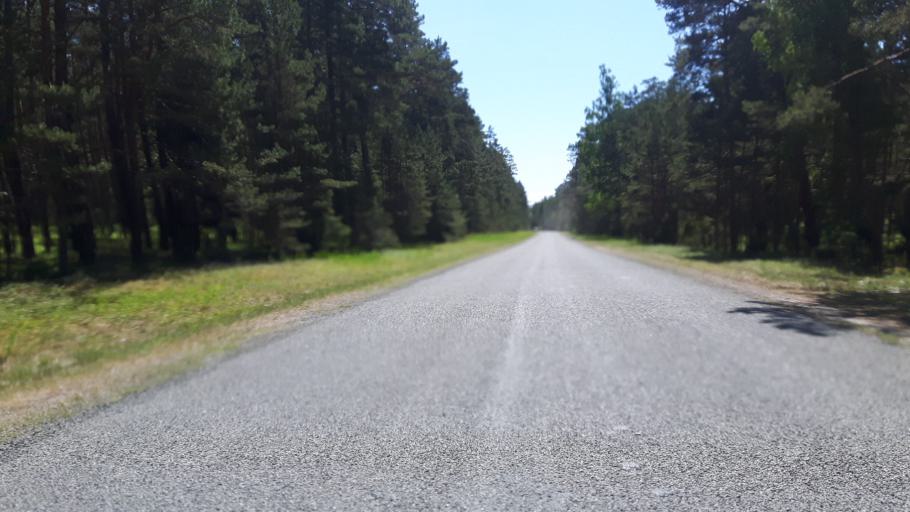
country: LV
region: Salacgrivas
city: Ainazi
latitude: 57.9790
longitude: 24.4152
